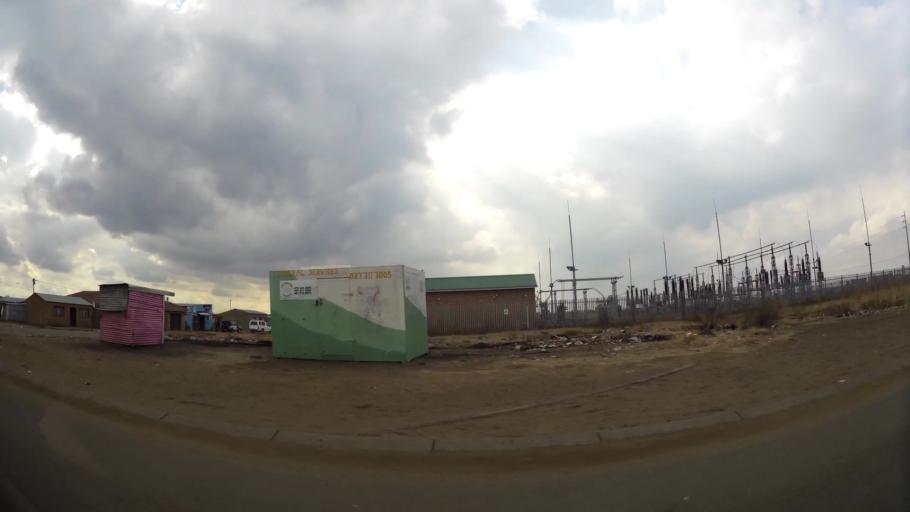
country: ZA
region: Orange Free State
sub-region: Fezile Dabi District Municipality
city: Sasolburg
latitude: -26.8560
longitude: 27.8865
